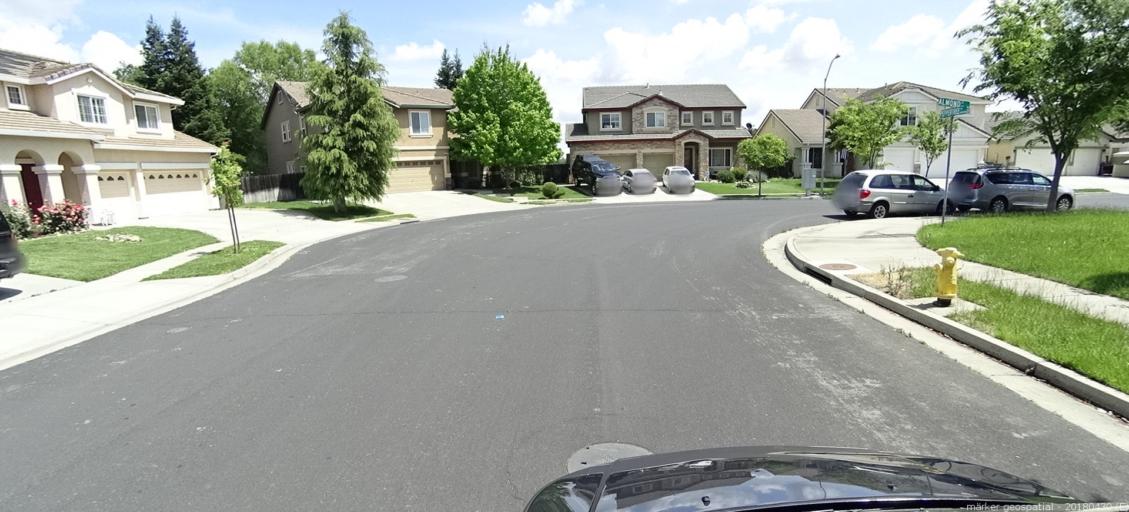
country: US
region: California
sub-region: Yolo County
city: West Sacramento
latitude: 38.5454
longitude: -121.5211
